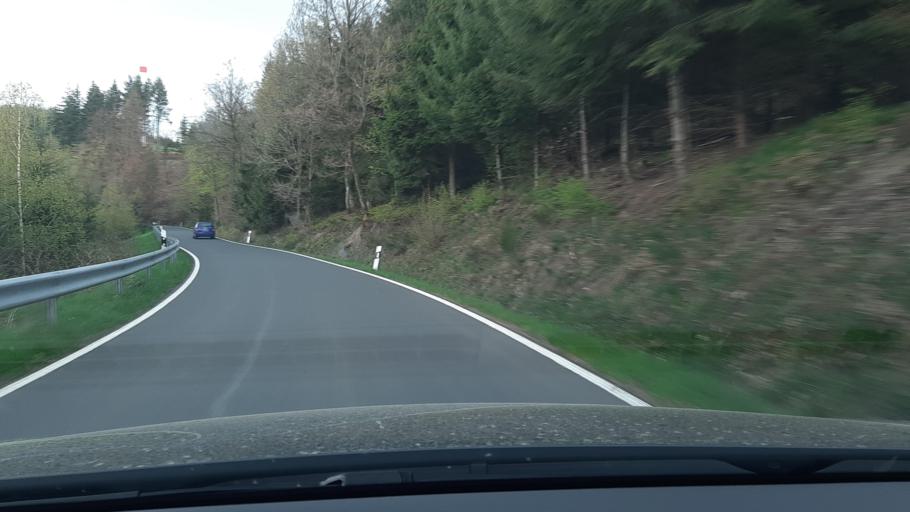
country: DE
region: North Rhine-Westphalia
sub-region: Regierungsbezirk Arnsberg
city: Bad Laasphe
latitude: 50.8918
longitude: 8.3858
